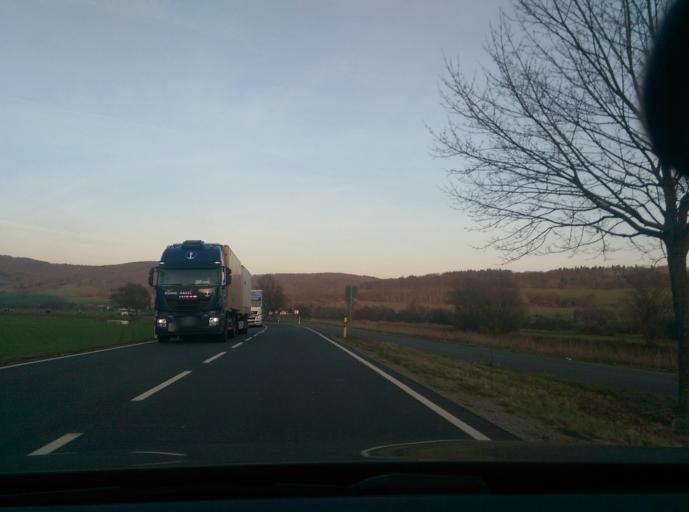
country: DE
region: Hesse
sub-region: Regierungsbezirk Kassel
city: Bad Sooden-Allendorf
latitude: 51.2832
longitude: 9.9655
